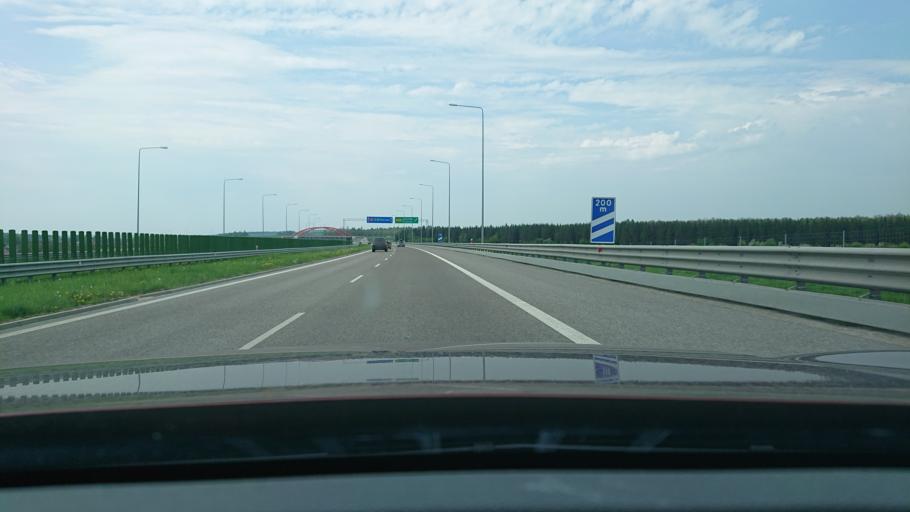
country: PL
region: Subcarpathian Voivodeship
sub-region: Powiat jaroslawski
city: Pawlosiow
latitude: 49.9677
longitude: 22.6532
